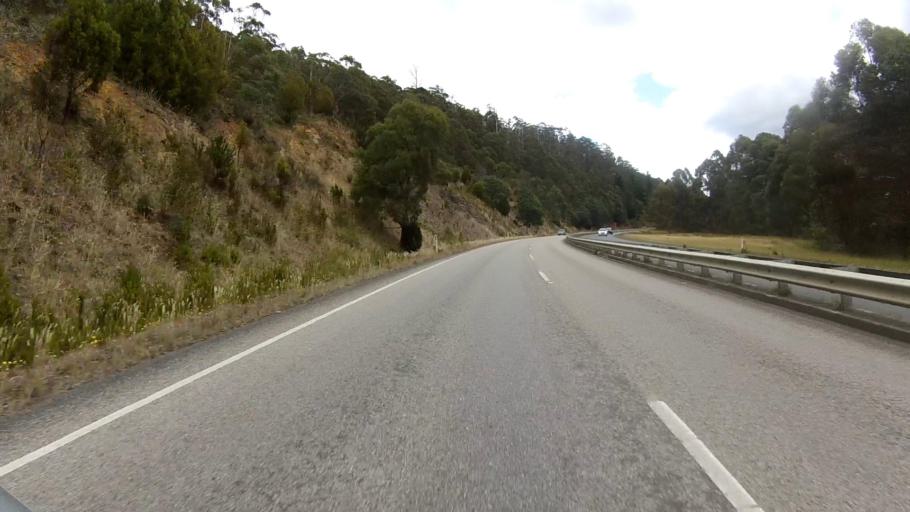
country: AU
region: Tasmania
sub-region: Kingborough
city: Margate
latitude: -42.9856
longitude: 147.1815
